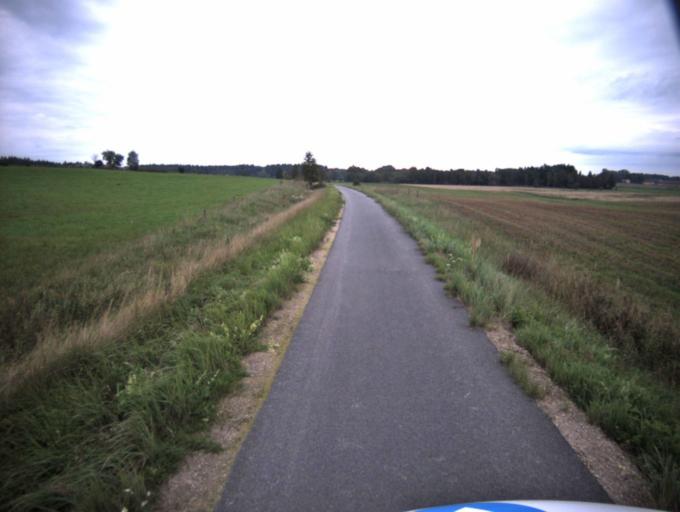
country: SE
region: Vaestra Goetaland
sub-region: Falkopings Kommun
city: Falkoeping
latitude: 57.9964
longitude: 13.5433
